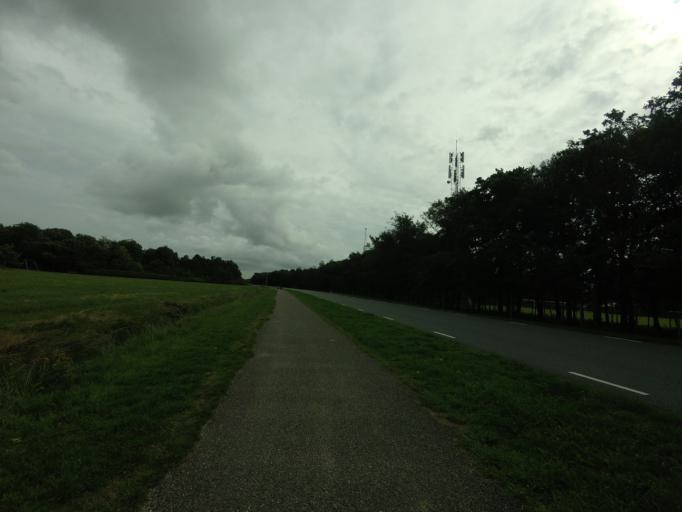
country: NL
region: Friesland
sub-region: Gemeente Ameland
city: Hollum
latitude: 53.4459
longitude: 5.6358
